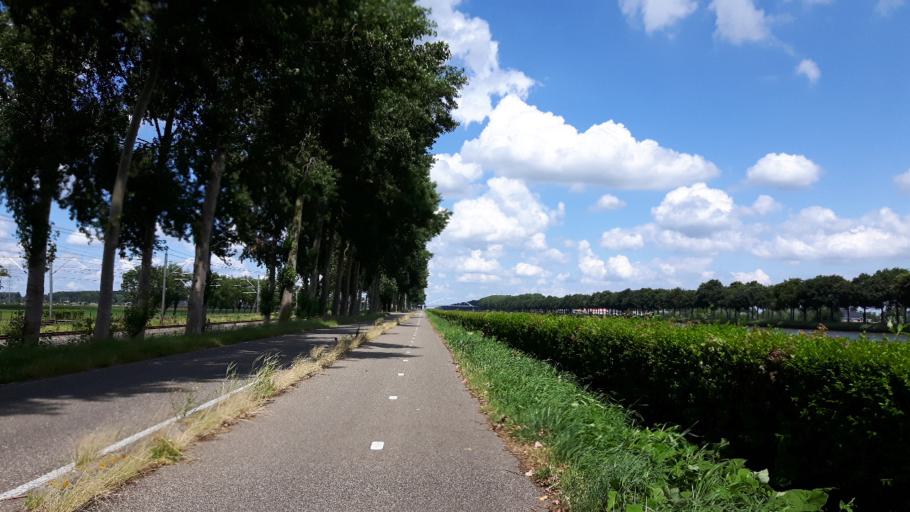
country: NL
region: Utrecht
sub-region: Stichtse Vecht
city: Vreeland
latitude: 52.2137
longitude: 5.0025
